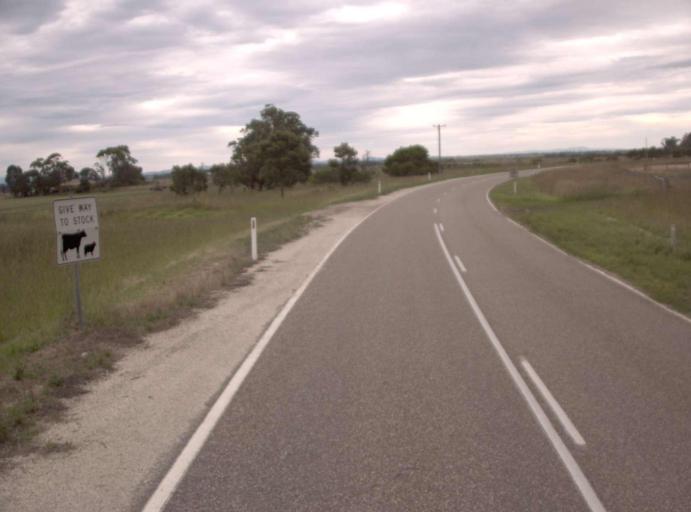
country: AU
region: Victoria
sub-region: Wellington
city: Sale
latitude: -38.0509
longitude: 147.1496
